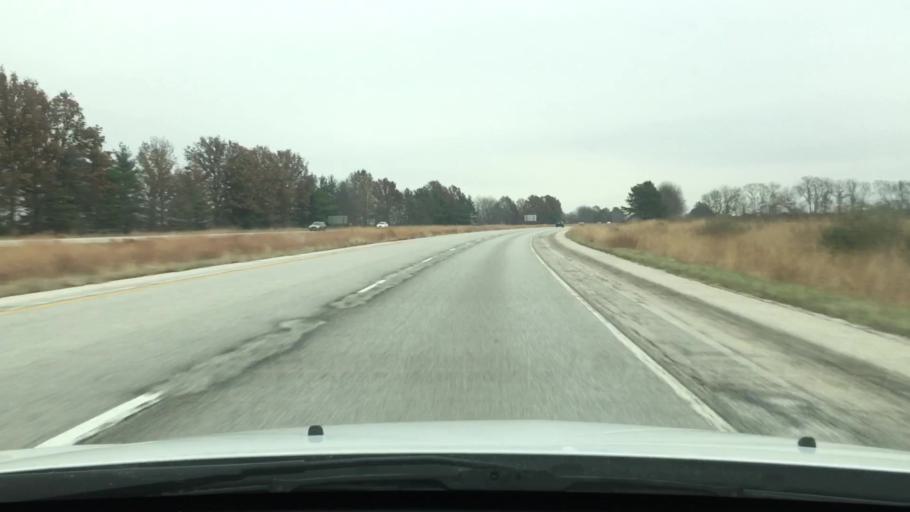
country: US
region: Illinois
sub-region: Morgan County
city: Jacksonville
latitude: 39.7371
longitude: -90.1494
